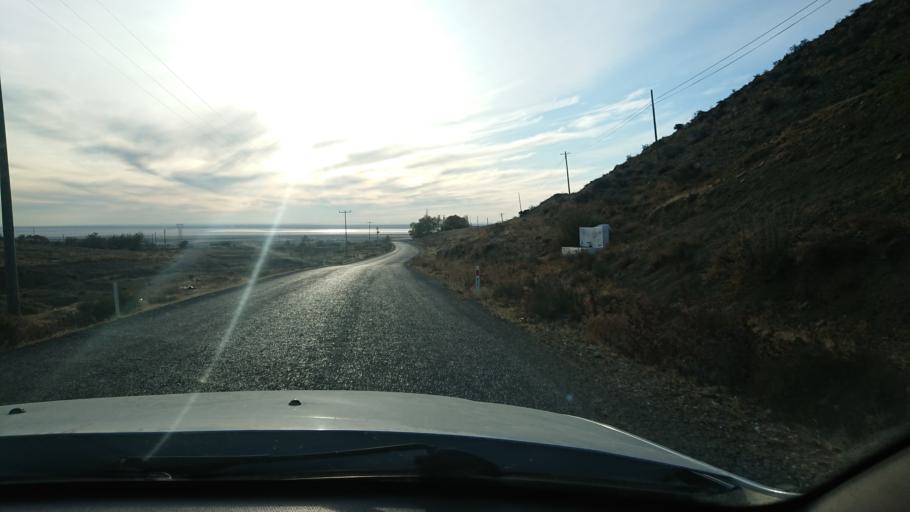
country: TR
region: Ankara
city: Sereflikochisar
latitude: 38.7467
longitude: 33.6836
